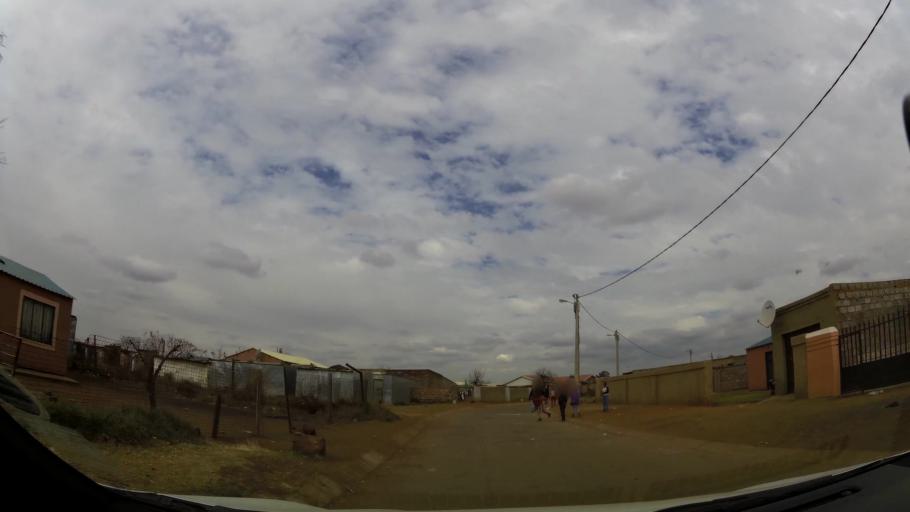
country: ZA
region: Gauteng
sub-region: Ekurhuleni Metropolitan Municipality
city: Germiston
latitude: -26.3866
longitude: 28.1344
